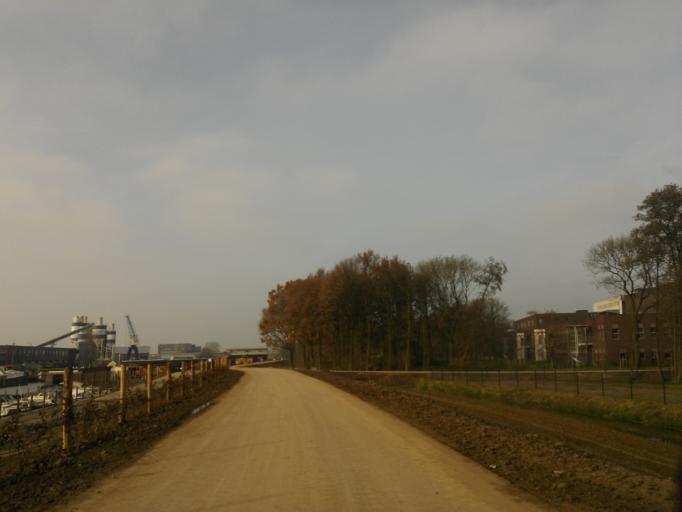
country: NL
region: Utrecht
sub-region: Gemeente Amersfoort
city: Hoogland
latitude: 52.1687
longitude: 5.3701
